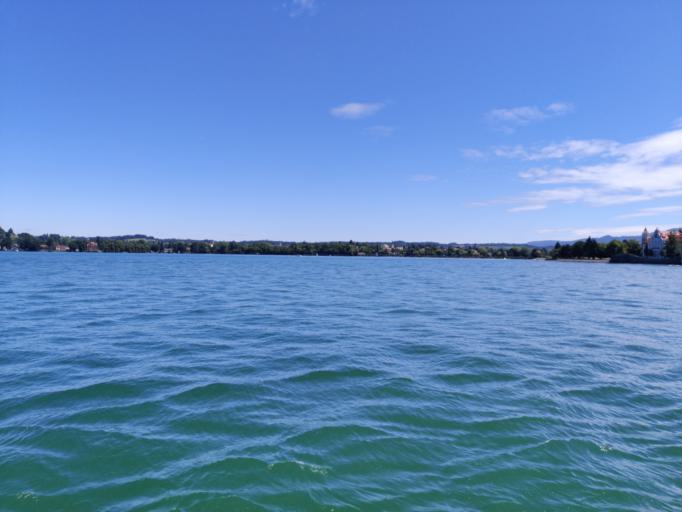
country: DE
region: Bavaria
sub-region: Swabia
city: Lindau
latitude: 47.5449
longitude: 9.6699
